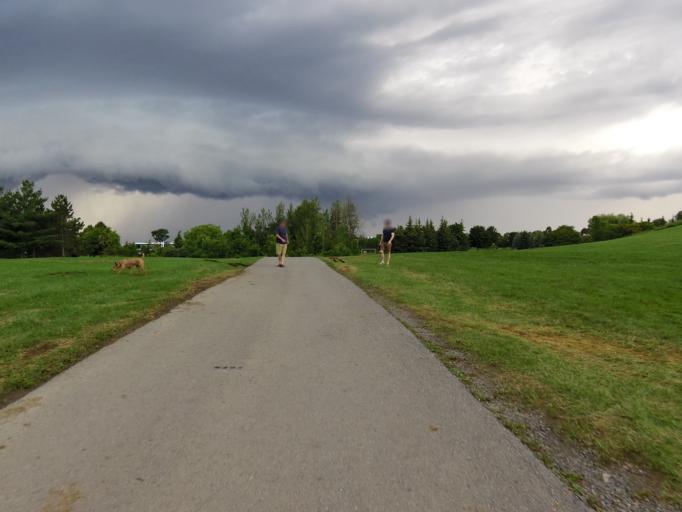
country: CA
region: Ontario
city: Bells Corners
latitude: 45.2956
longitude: -75.9025
